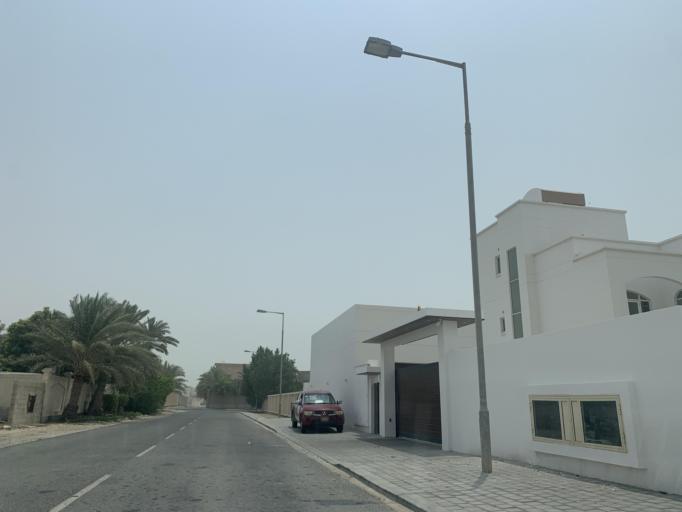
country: BH
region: Central Governorate
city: Madinat Hamad
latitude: 26.1676
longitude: 50.4791
